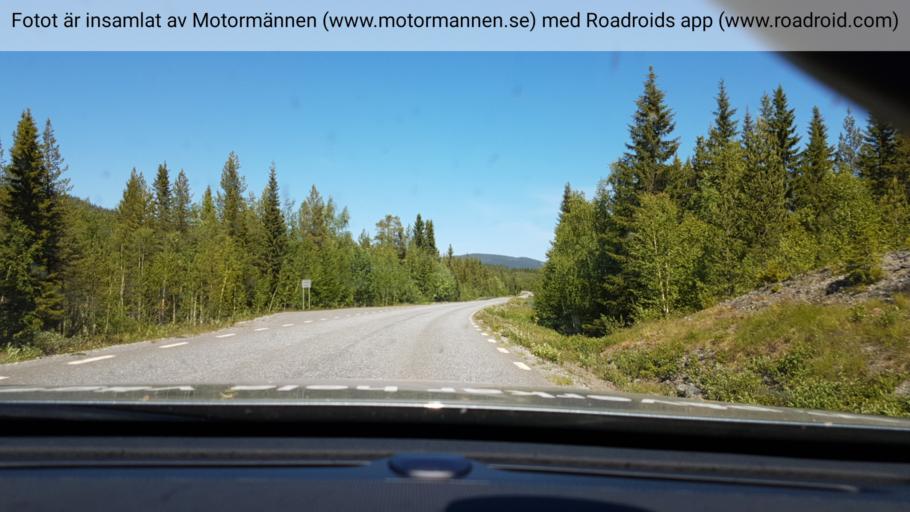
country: SE
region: Vaesterbotten
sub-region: Vilhelmina Kommun
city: Sjoberg
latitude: 64.8975
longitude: 15.8586
